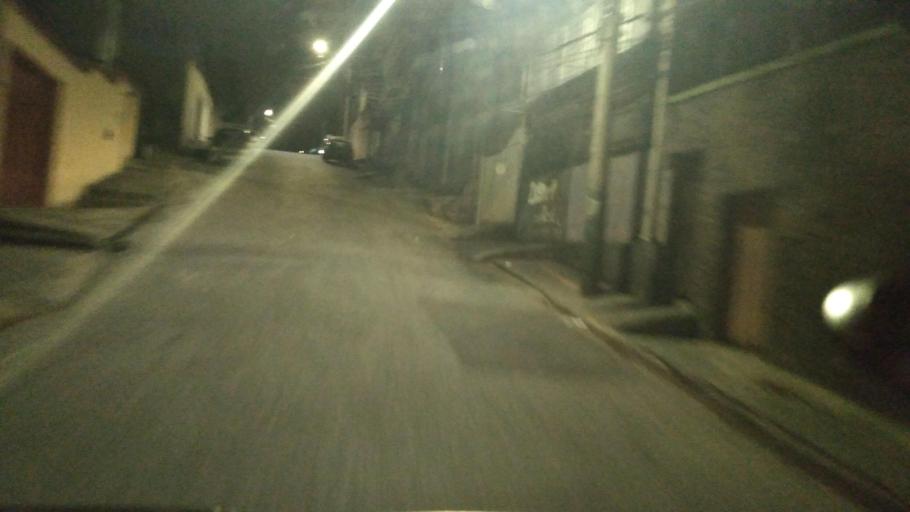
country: BR
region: Minas Gerais
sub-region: Belo Horizonte
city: Belo Horizonte
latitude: -19.8877
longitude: -43.9630
